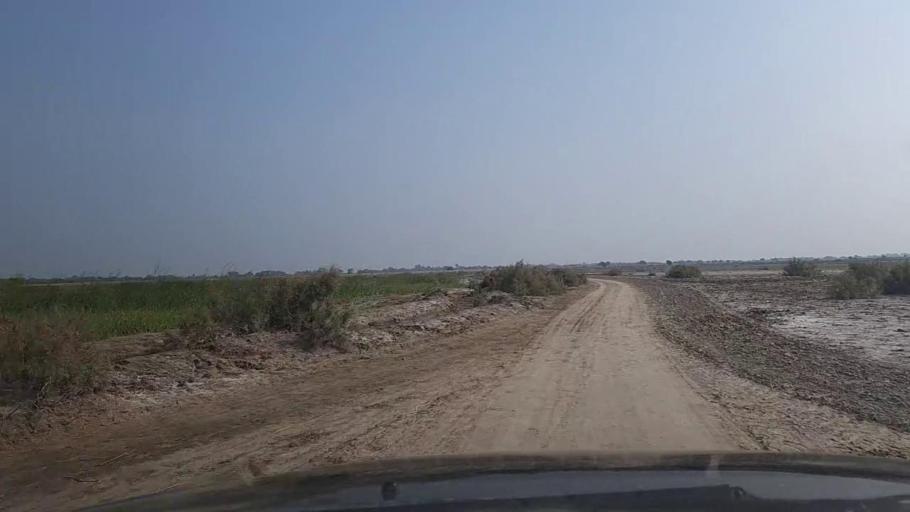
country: PK
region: Sindh
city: Mirpur Batoro
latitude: 24.6772
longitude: 68.2451
